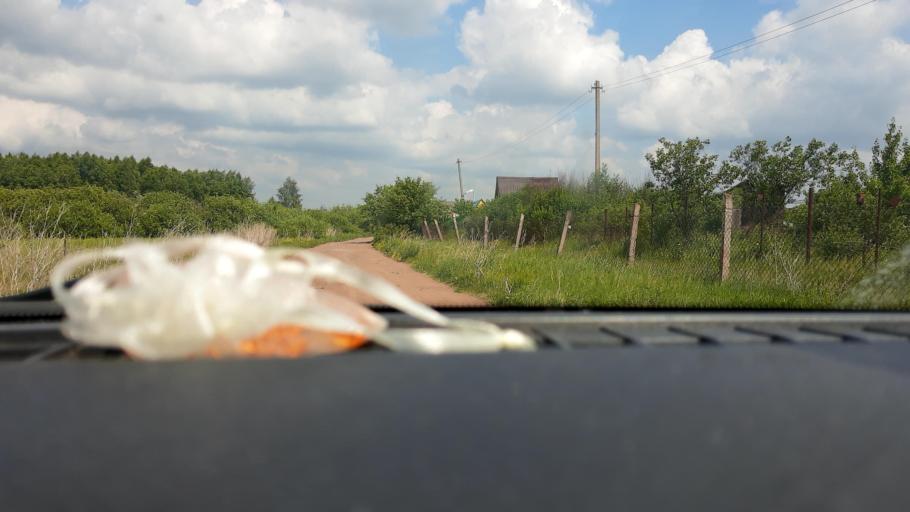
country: RU
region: Bashkortostan
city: Asanovo
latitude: 54.9180
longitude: 55.6283
